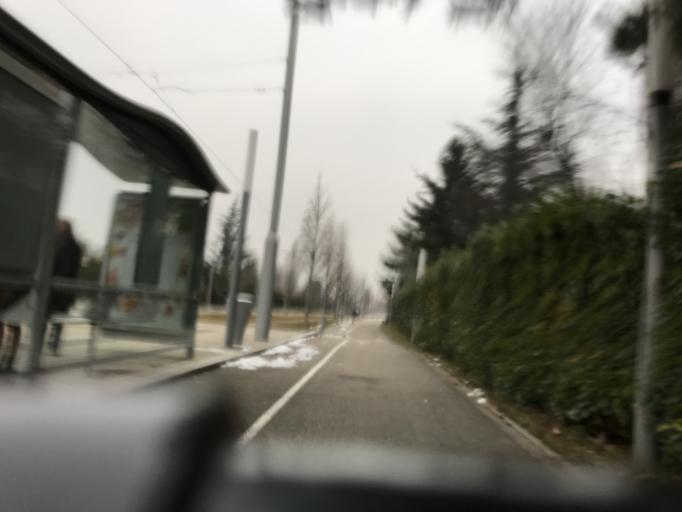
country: FR
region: Rhone-Alpes
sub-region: Departement de l'Isere
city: Seyssinet-Pariset
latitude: 45.1721
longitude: 5.6943
